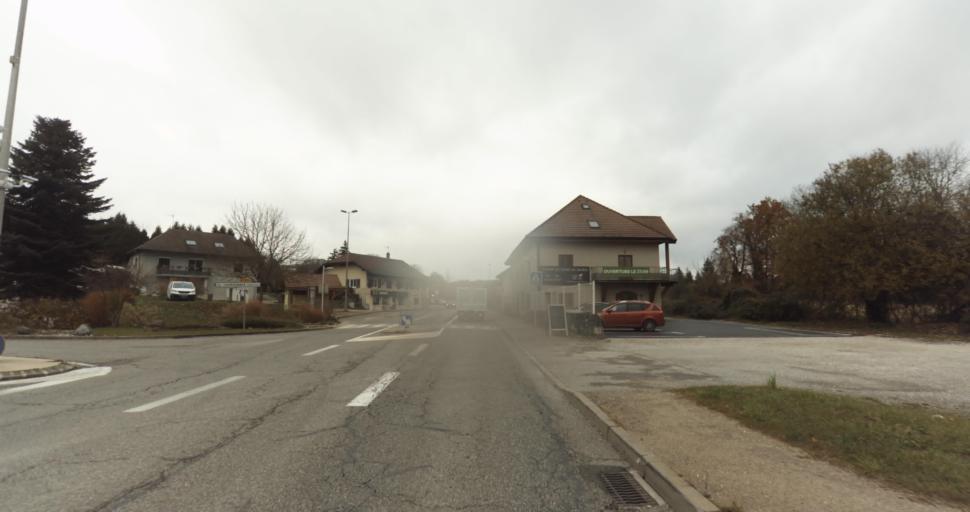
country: FR
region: Rhone-Alpes
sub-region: Departement de la Haute-Savoie
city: Saint-Martin-Bellevue
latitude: 45.9772
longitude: 6.1642
